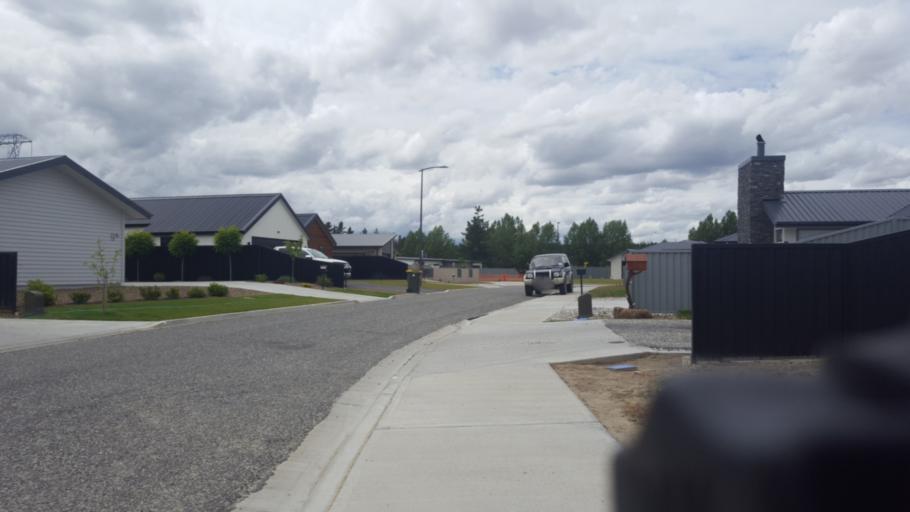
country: NZ
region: Otago
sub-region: Queenstown-Lakes District
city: Wanaka
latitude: -45.2427
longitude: 169.3751
